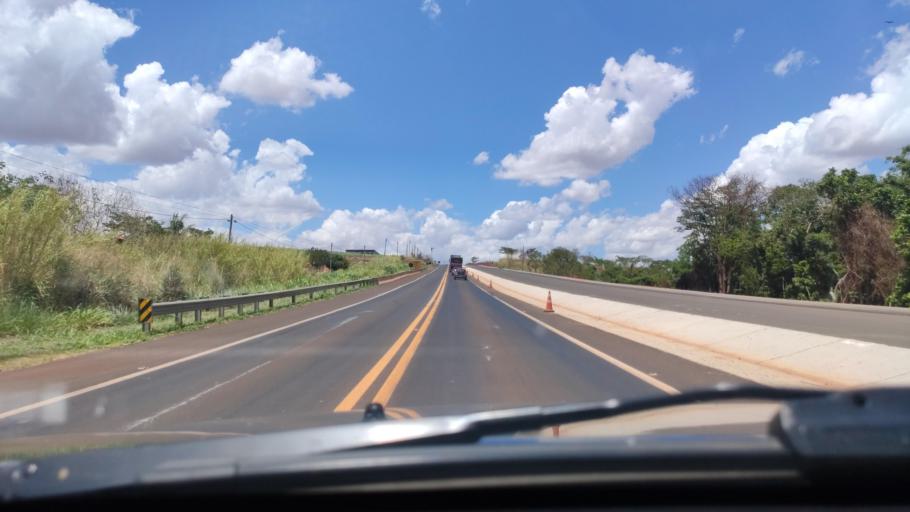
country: BR
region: Sao Paulo
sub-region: Jau
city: Jau
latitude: -22.2353
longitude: -48.5355
